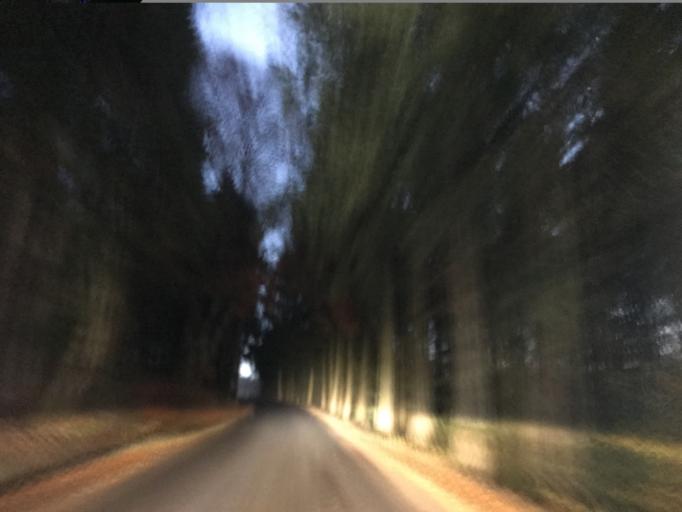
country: FR
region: Rhone-Alpes
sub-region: Departement de la Loire
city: Noiretable
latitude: 45.7581
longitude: 3.6979
